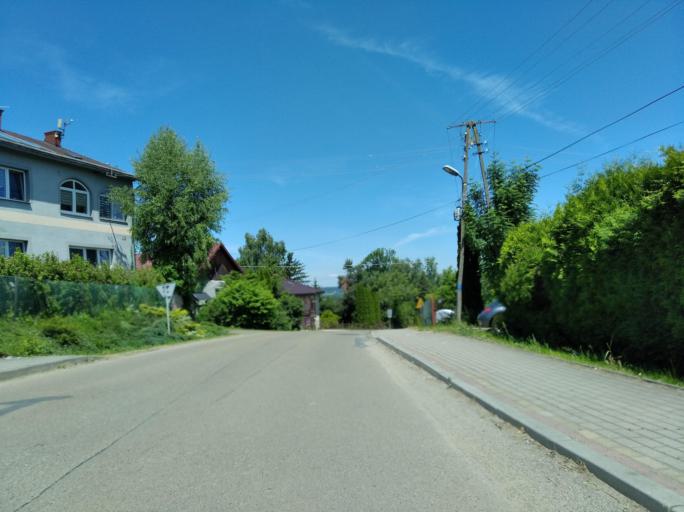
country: PL
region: Subcarpathian Voivodeship
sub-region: Powiat jasielski
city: Tarnowiec
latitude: 49.7149
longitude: 21.5537
